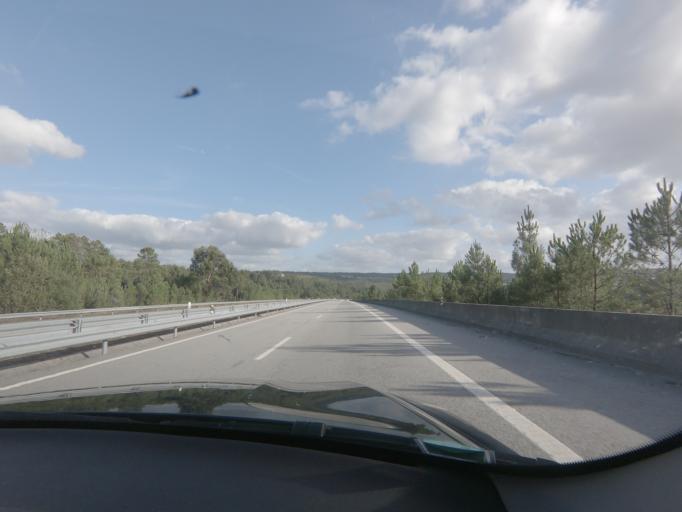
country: PT
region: Viseu
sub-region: Viseu
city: Campo
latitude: 40.7632
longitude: -7.9234
